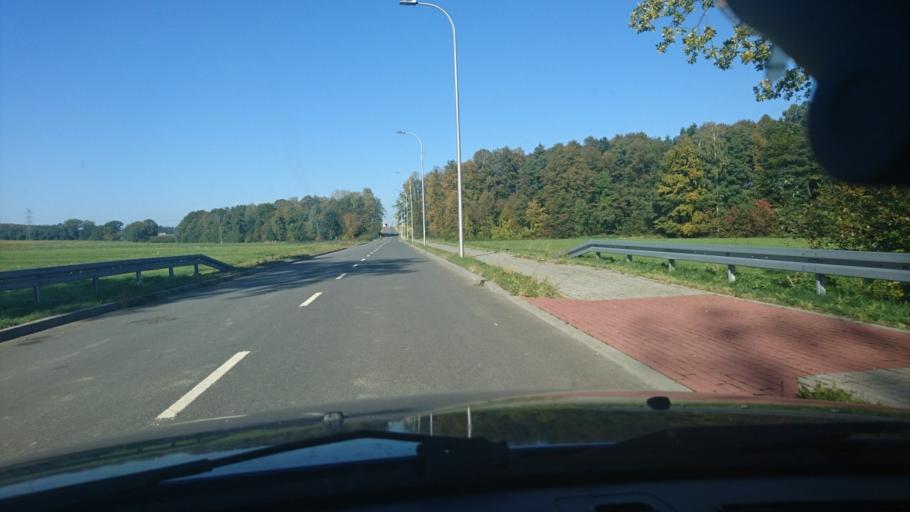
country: PL
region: Silesian Voivodeship
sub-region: Powiat bielski
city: Bronow
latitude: 49.8597
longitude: 18.9437
